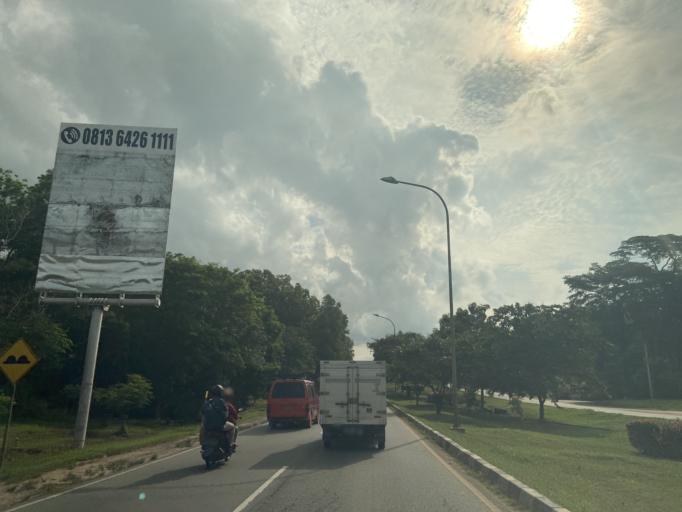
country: SG
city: Singapore
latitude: 1.0988
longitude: 104.0638
